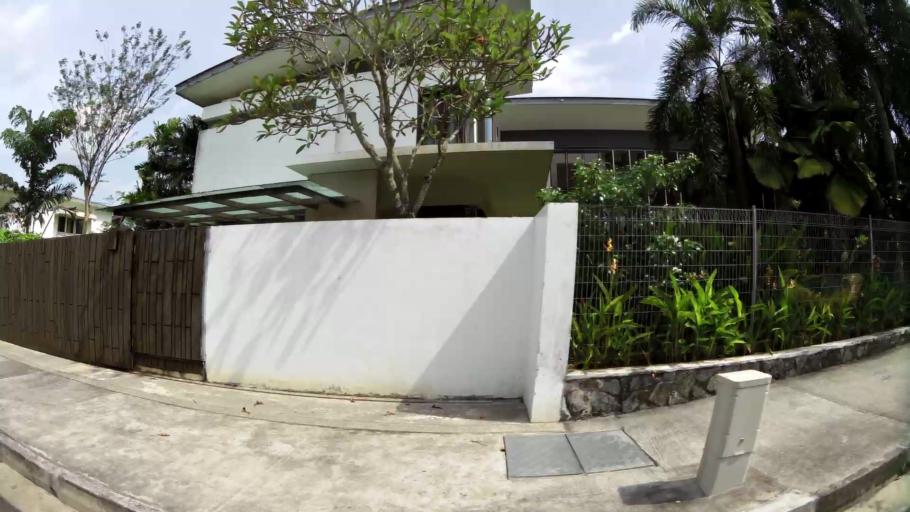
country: SG
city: Singapore
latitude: 1.3252
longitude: 103.7675
